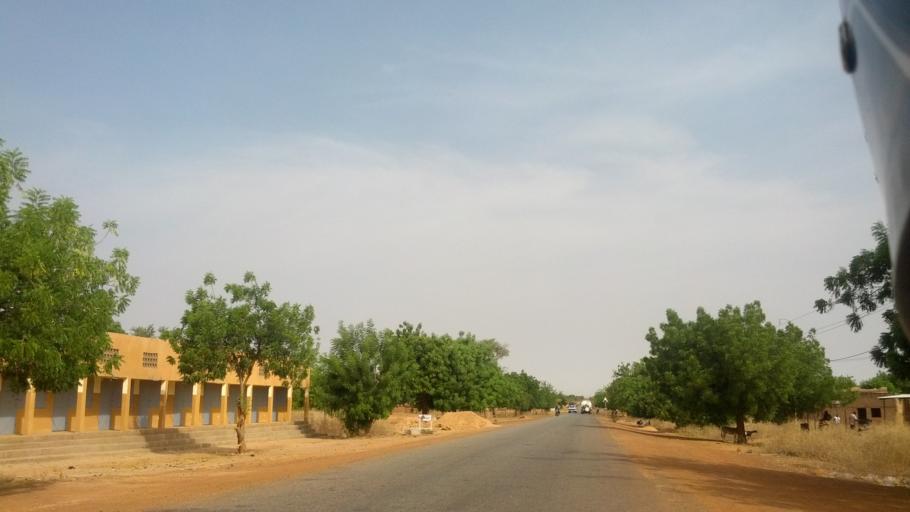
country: BF
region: Centre-Nord
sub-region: Province du Sanmatenga
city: Kaya
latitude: 12.9130
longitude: -1.0780
